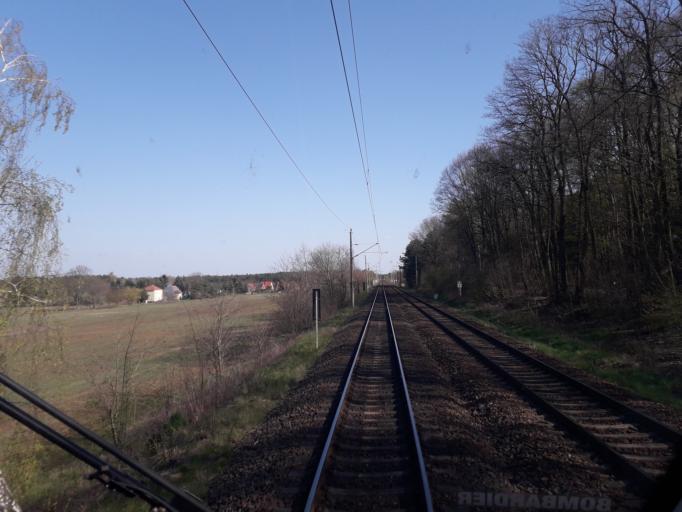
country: DE
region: Brandenburg
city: Michendorf
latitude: 52.3325
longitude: 13.0991
